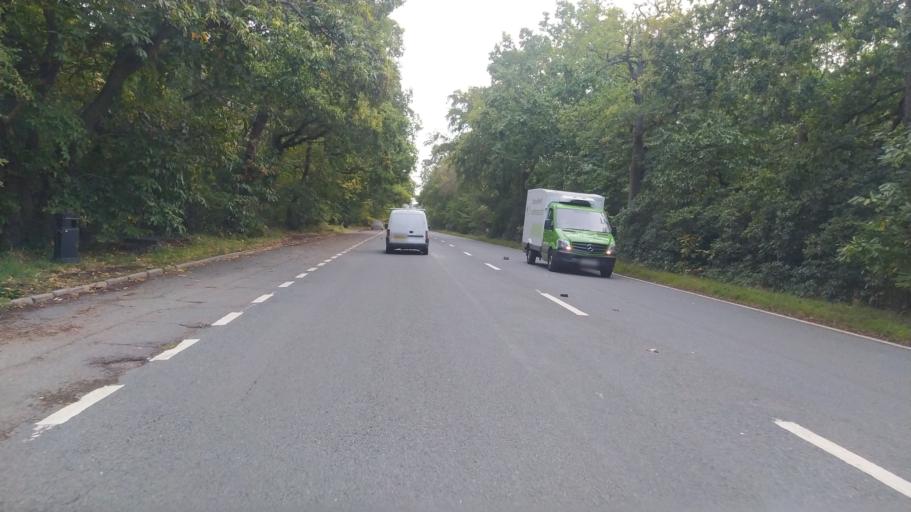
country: GB
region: England
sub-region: Hampshire
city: Eversley
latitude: 51.3191
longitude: -0.8771
